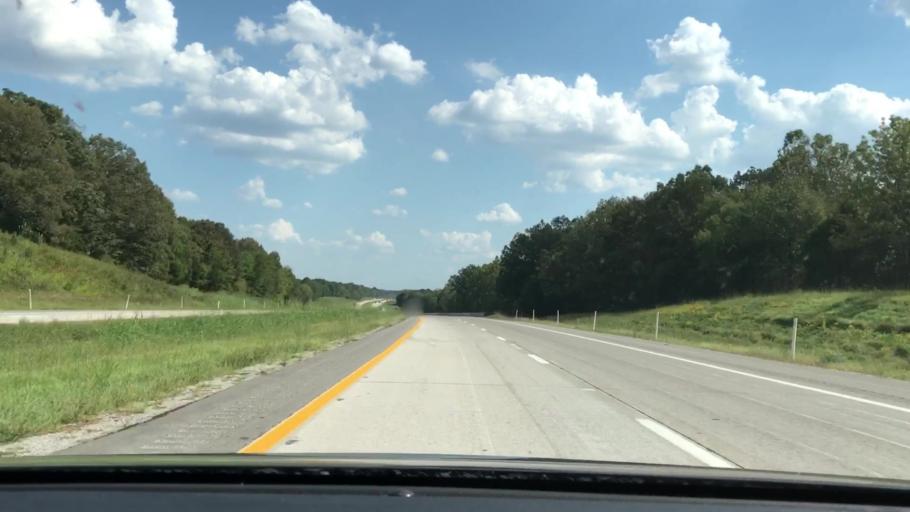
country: US
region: Kentucky
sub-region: Ohio County
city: Oak Grove
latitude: 37.3493
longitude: -86.7828
